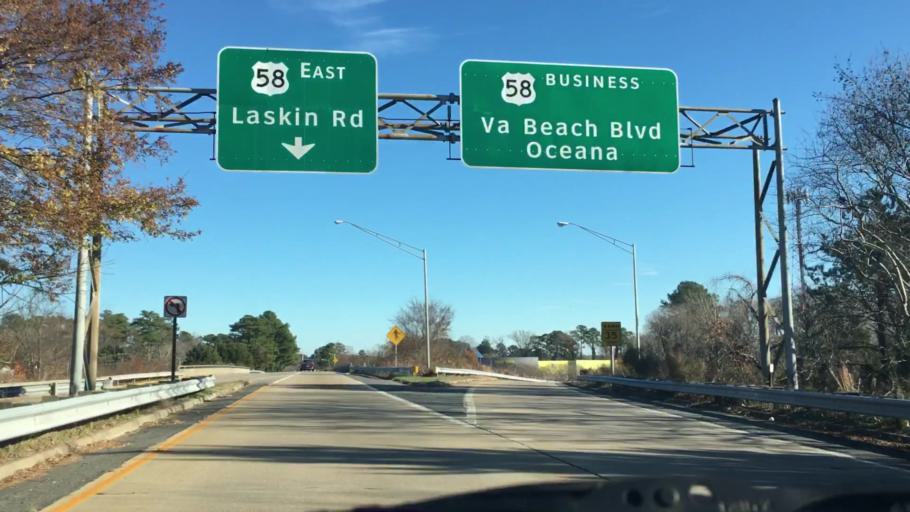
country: US
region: Virginia
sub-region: City of Virginia Beach
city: Virginia Beach
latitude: 36.8431
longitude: -76.0404
